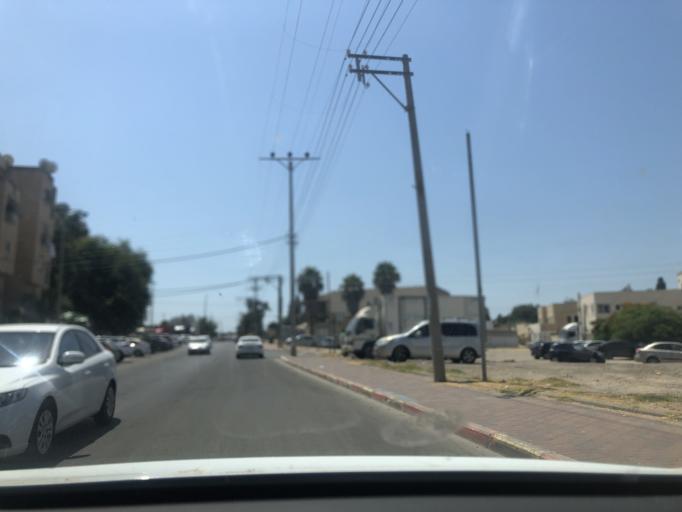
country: IL
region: Central District
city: Lod
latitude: 31.9569
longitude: 34.9014
